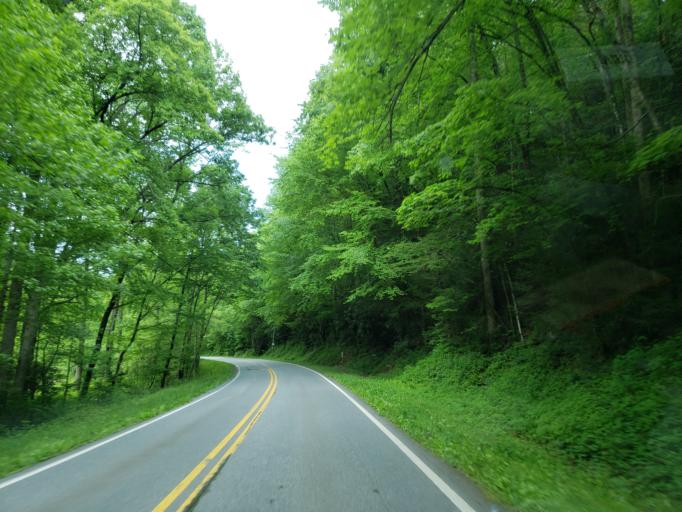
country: US
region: Georgia
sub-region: Fannin County
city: Blue Ridge
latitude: 34.8413
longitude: -84.3968
